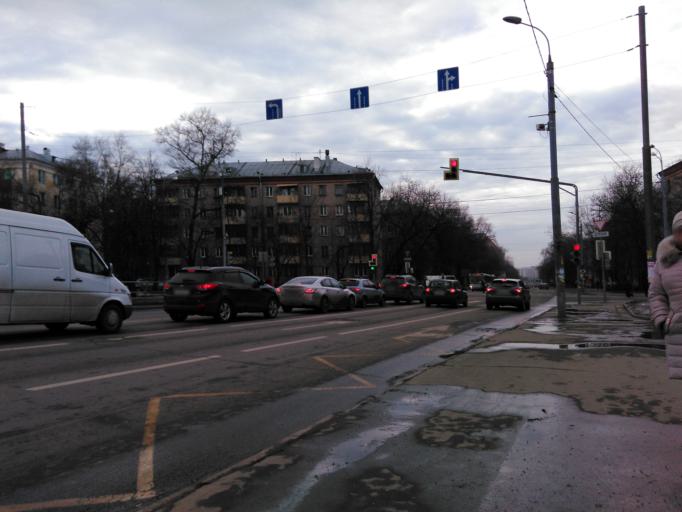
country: RU
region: Moscow
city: Vatutino
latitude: 55.8679
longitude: 37.6762
